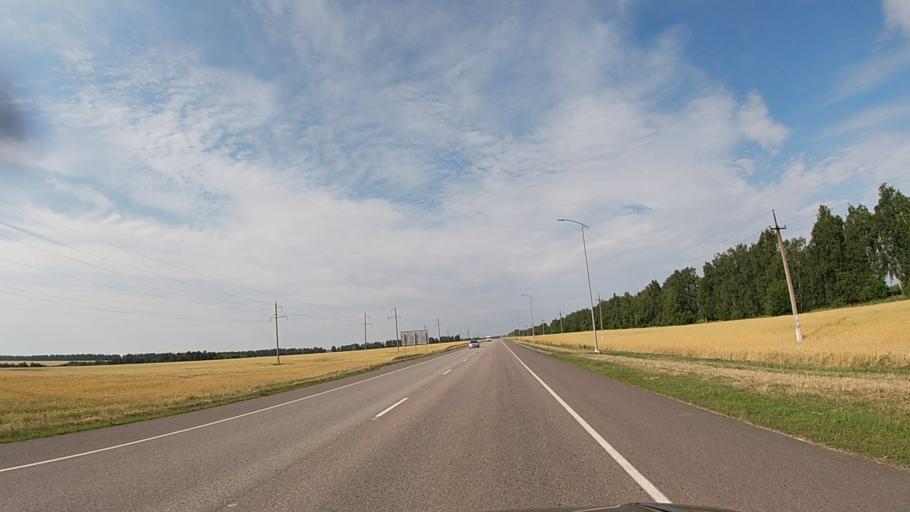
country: RU
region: Belgorod
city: Proletarskiy
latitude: 50.8293
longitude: 35.7639
